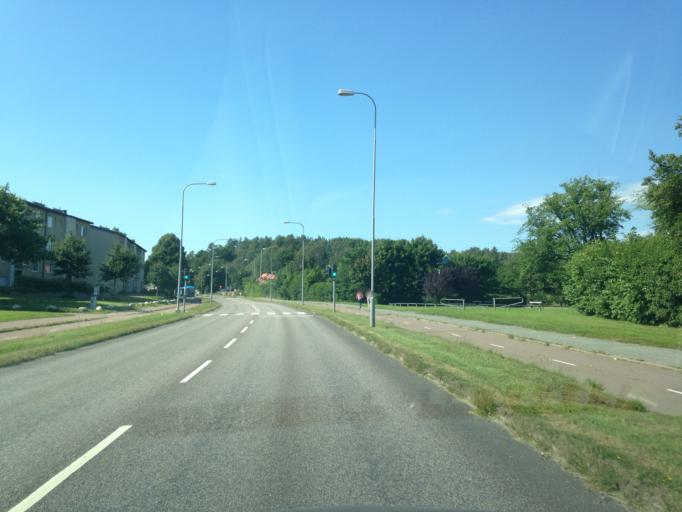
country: SE
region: Vaestra Goetaland
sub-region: Goteborg
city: Majorna
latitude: 57.7188
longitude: 11.9076
